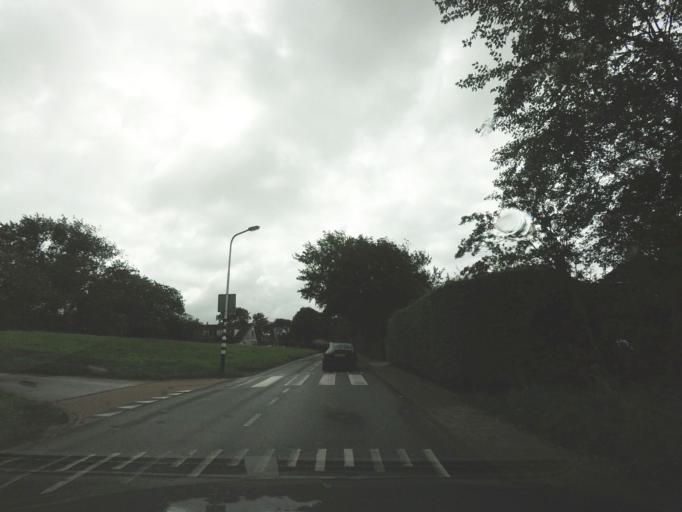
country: NL
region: North Holland
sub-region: Gemeente Bergen
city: Egmond aan Zee
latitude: 52.7239
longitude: 4.6602
